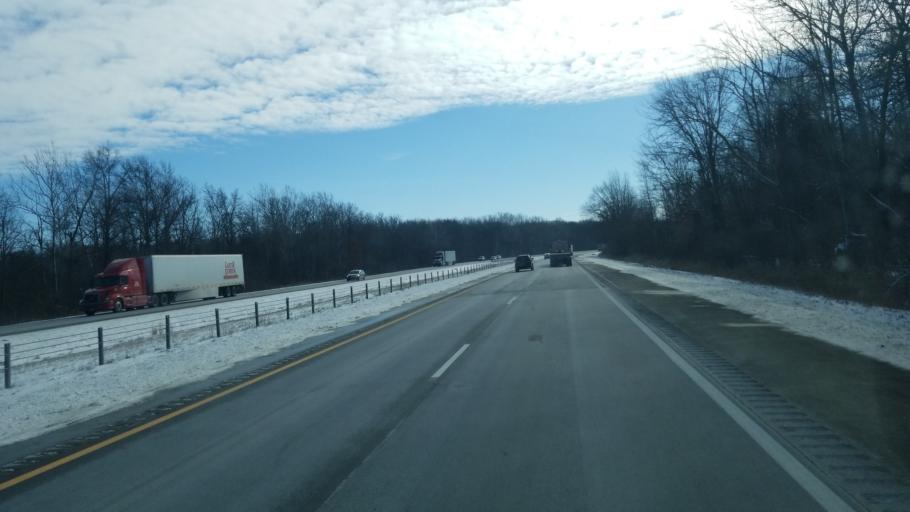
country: US
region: Michigan
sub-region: Washtenaw County
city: Milan
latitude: 42.0468
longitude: -83.6700
